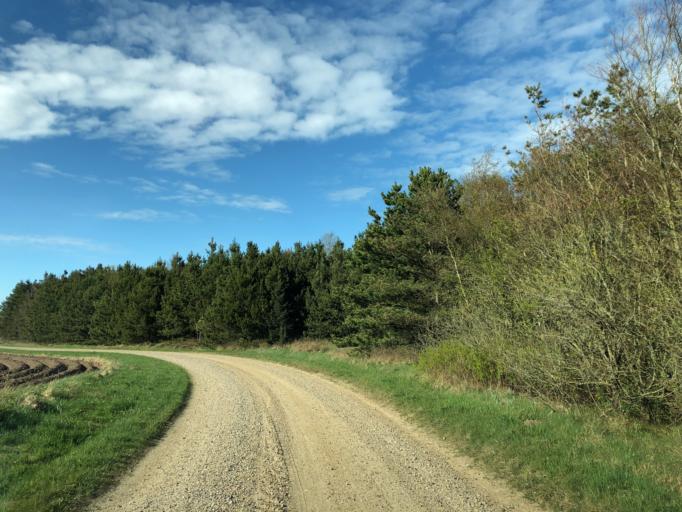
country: DK
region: Central Jutland
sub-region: Holstebro Kommune
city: Ulfborg
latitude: 56.2631
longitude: 8.3281
